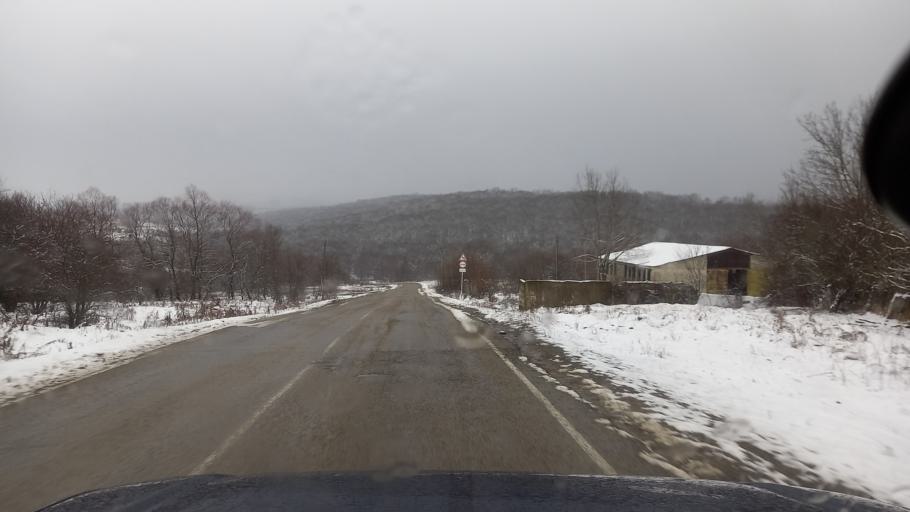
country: RU
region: Adygeya
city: Abadzekhskaya
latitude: 44.3578
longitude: 40.4070
